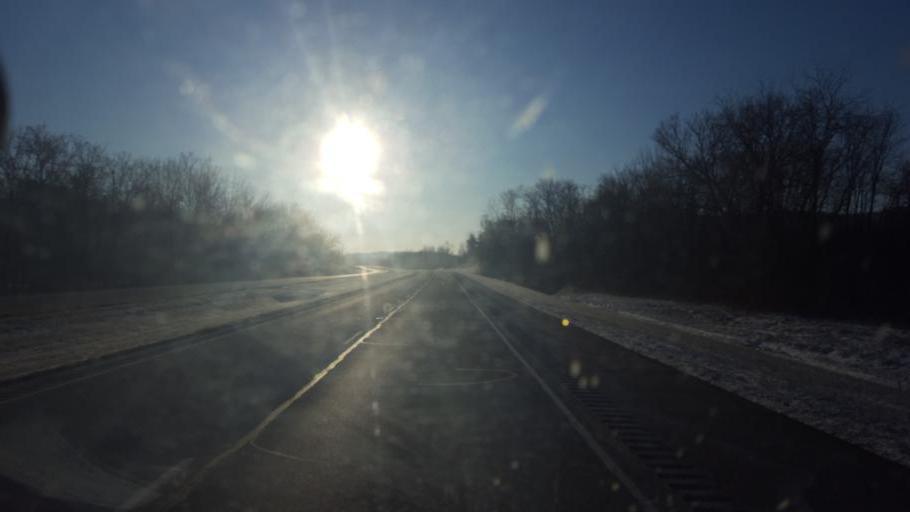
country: US
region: Ohio
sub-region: Pike County
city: Piketon
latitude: 39.0544
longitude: -83.0643
